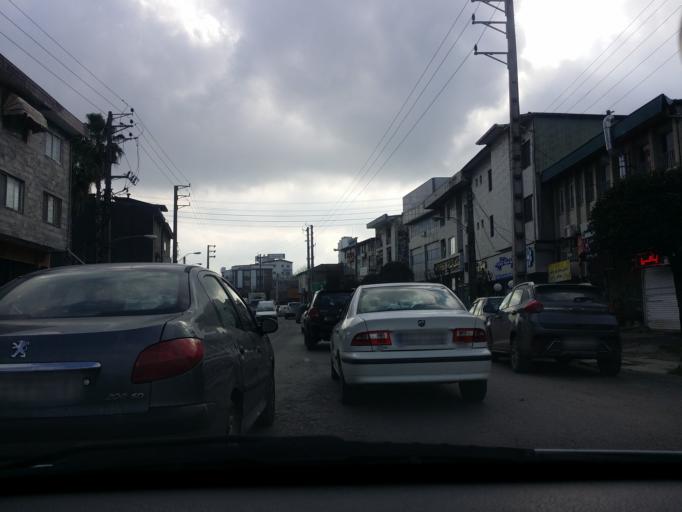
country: IR
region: Mazandaran
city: Chalus
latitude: 36.6588
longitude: 51.4145
